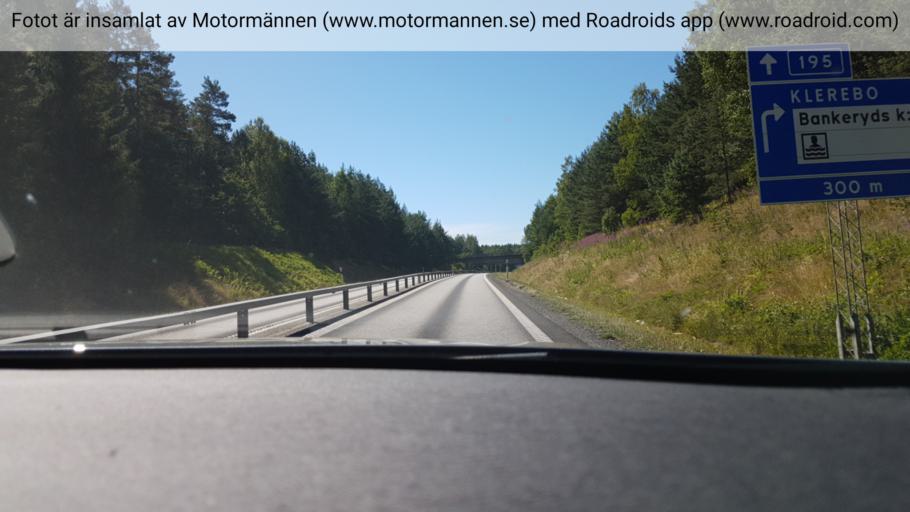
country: SE
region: Joenkoeping
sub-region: Jonkopings Kommun
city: Bankeryd
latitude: 57.8571
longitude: 14.1039
